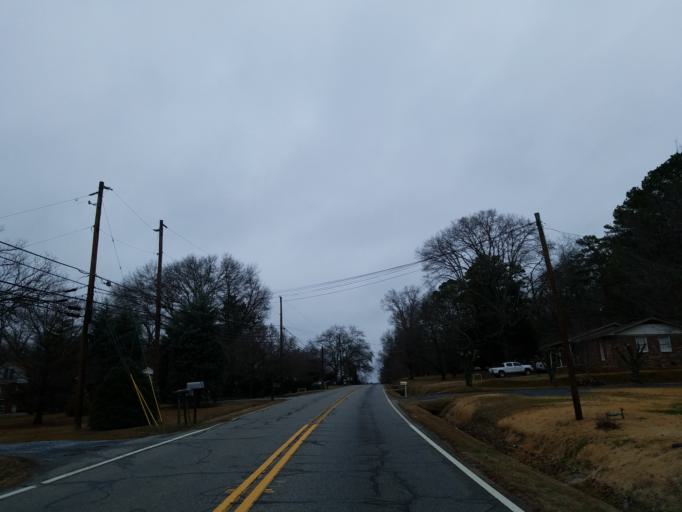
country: US
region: Georgia
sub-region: Bartow County
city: Cartersville
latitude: 34.1922
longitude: -84.8217
